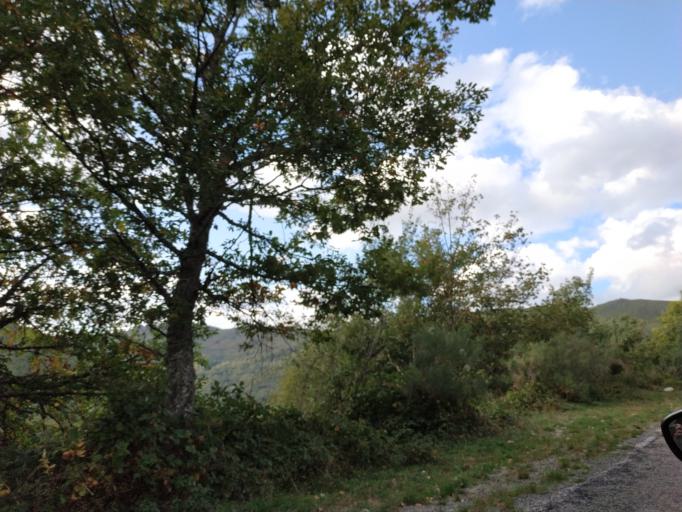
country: ES
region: Castille and Leon
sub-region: Provincia de Leon
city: Candin
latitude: 42.8617
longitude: -6.8536
